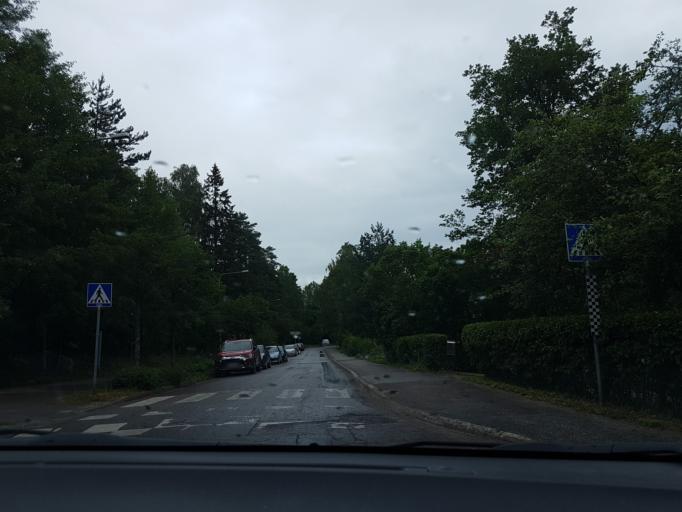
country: FI
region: Uusimaa
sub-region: Helsinki
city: Vantaa
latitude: 60.2406
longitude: 25.0920
